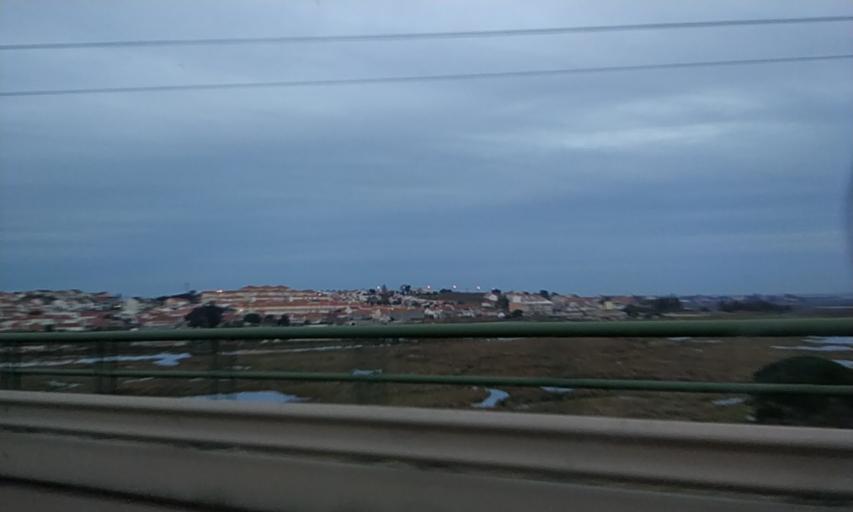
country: PT
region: Setubal
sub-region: Setubal
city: Setubal
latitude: 38.5121
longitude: -8.8384
